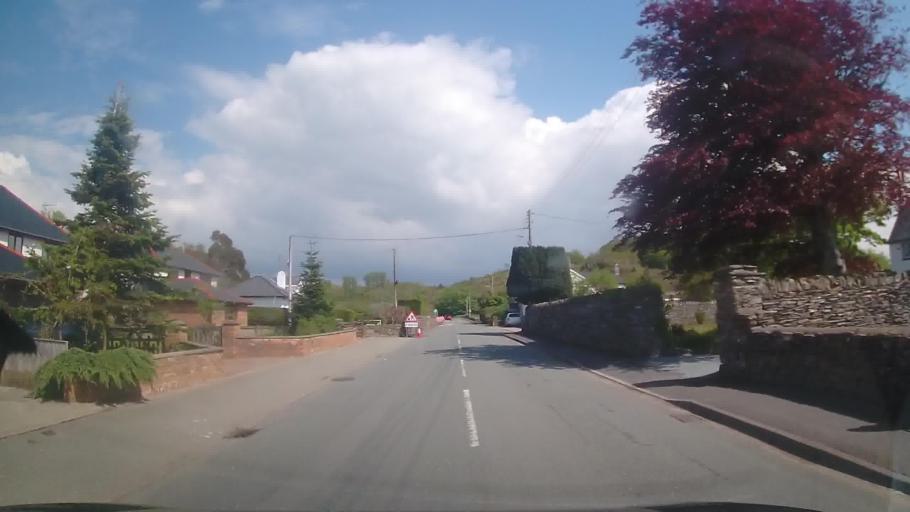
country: GB
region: Wales
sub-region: Gwynedd
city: Porthmadog
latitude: 52.9140
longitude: -4.1585
